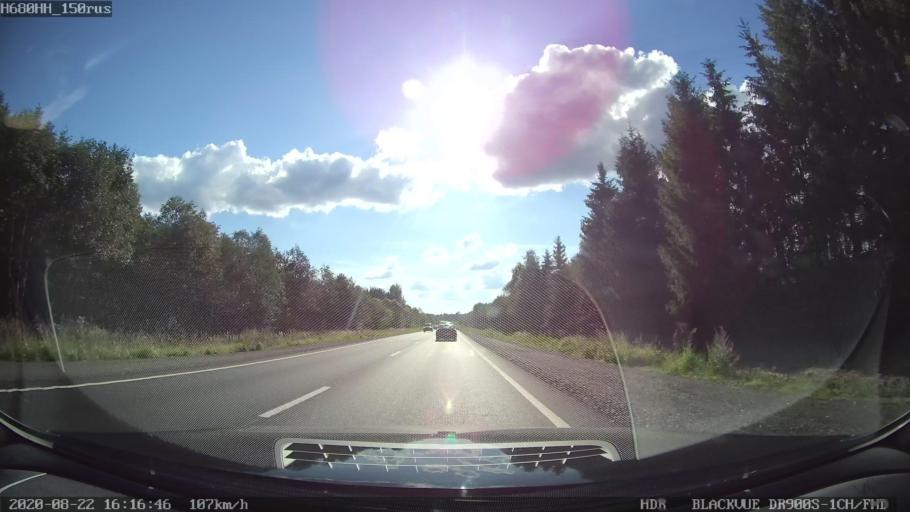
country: RU
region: Tverskaya
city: Rameshki
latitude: 57.4311
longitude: 36.1718
